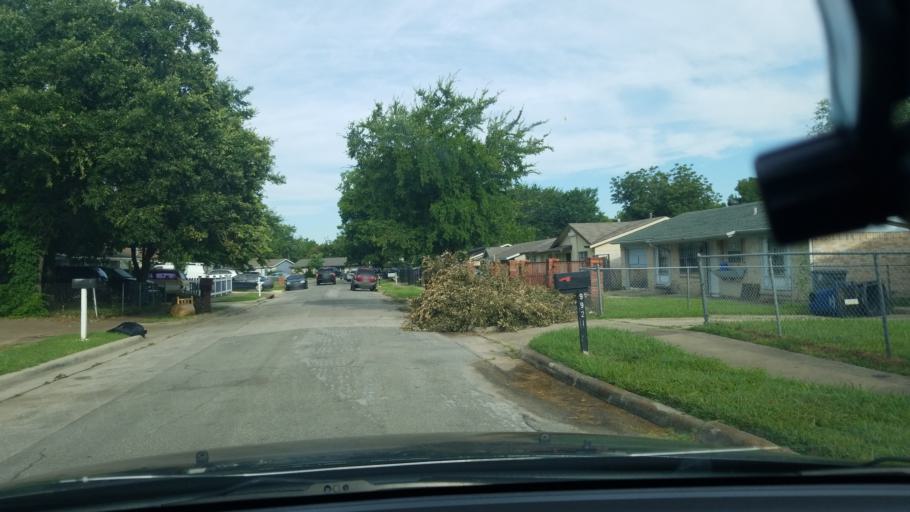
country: US
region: Texas
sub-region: Dallas County
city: Balch Springs
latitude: 32.7537
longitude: -96.6505
